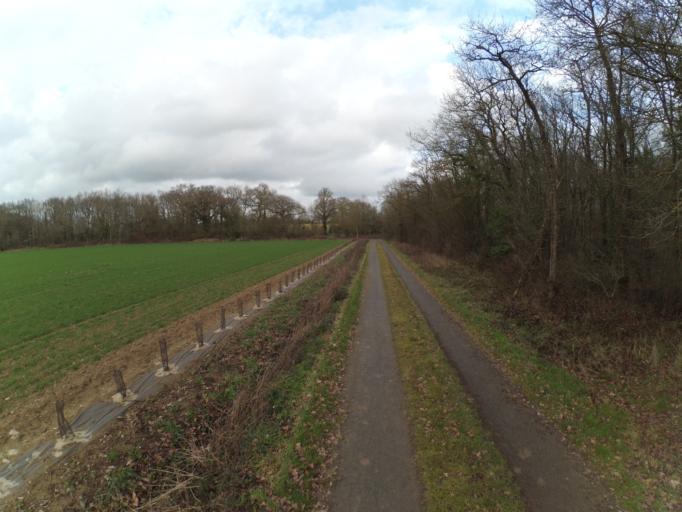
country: FR
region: Pays de la Loire
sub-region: Departement de la Vendee
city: Saint-Hilaire-de-Loulay
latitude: 47.0187
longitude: -1.2992
